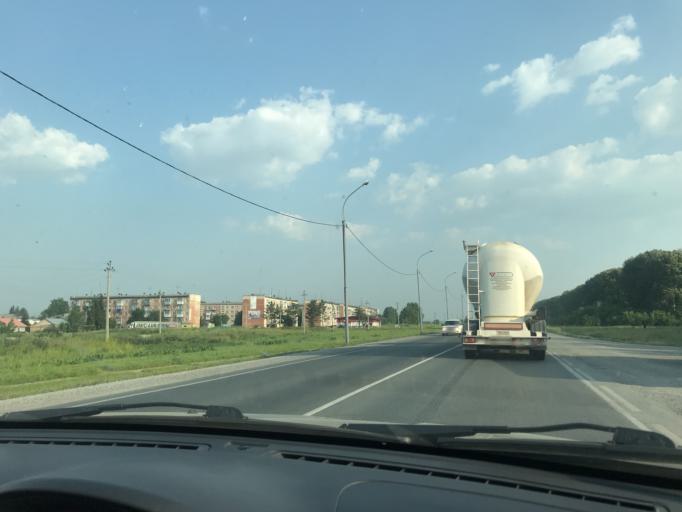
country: RU
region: Novosibirsk
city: Linevo
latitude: 54.5101
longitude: 83.3318
